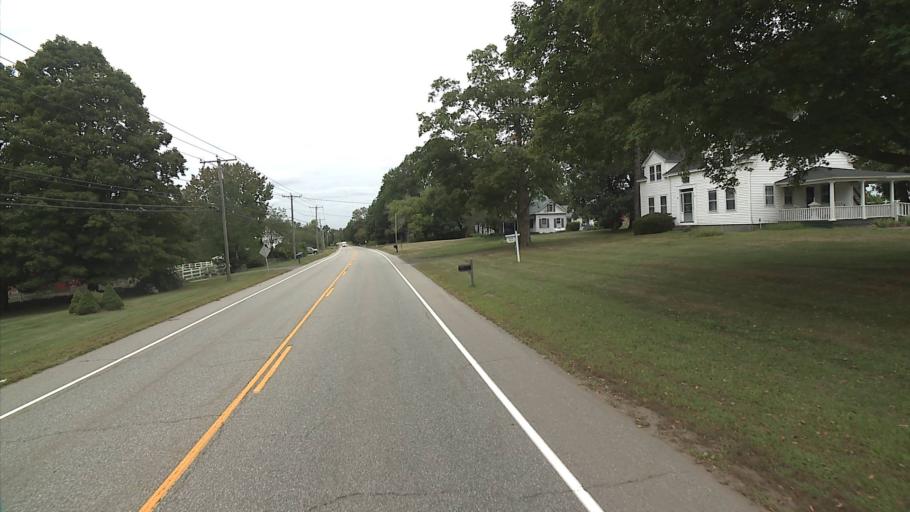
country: US
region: Connecticut
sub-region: Tolland County
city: Hebron
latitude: 41.6804
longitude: -72.4133
